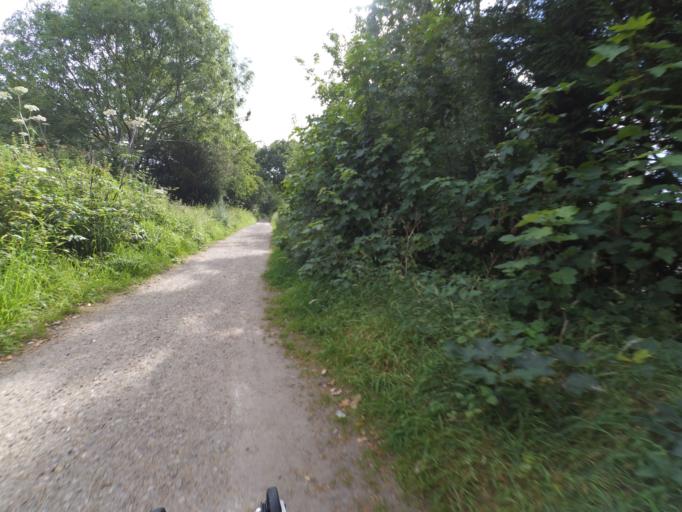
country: GB
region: England
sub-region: Staffordshire
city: Gnosall
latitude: 52.7825
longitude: -2.2659
